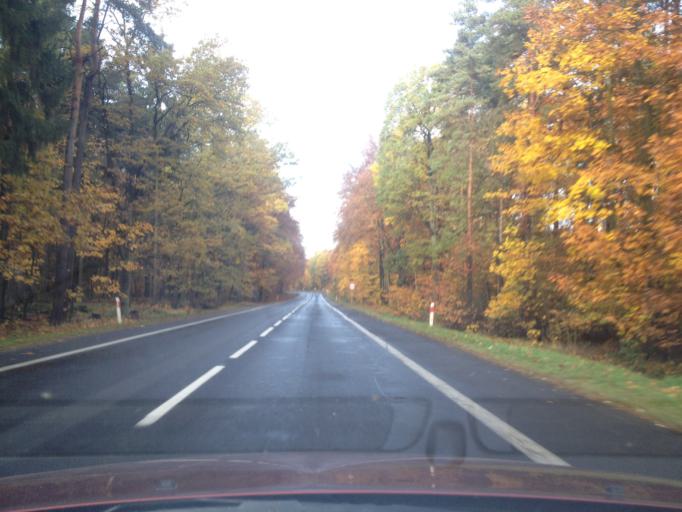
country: PL
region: Lower Silesian Voivodeship
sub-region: Powiat lubanski
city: Siekierczyn
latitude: 51.1589
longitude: 15.1499
